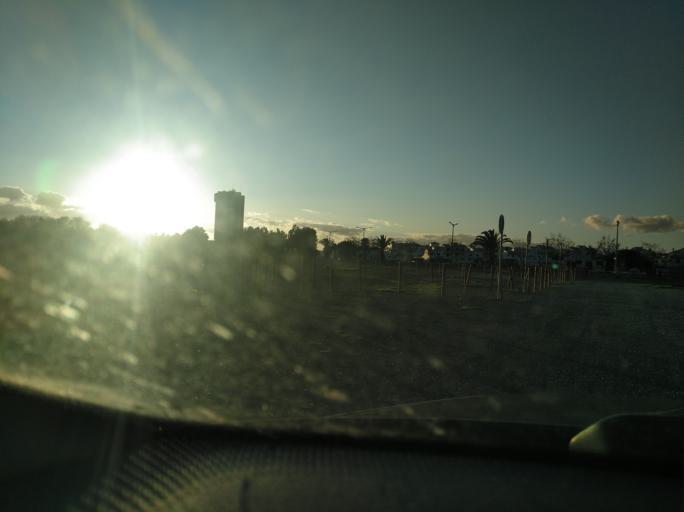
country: PT
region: Faro
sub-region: Vila Real de Santo Antonio
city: Monte Gordo
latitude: 37.1746
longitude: -7.4925
